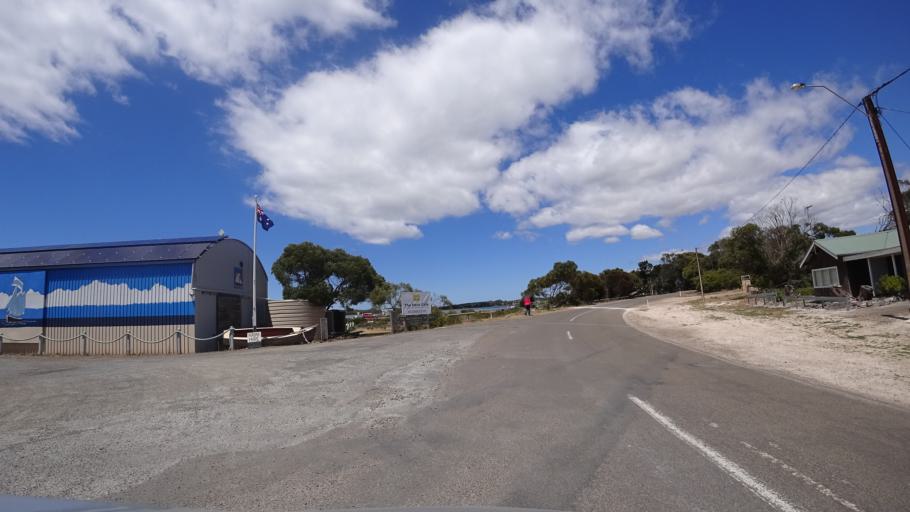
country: AU
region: South Australia
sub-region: Kangaroo Island
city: Kingscote
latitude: -35.7864
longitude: 137.7725
